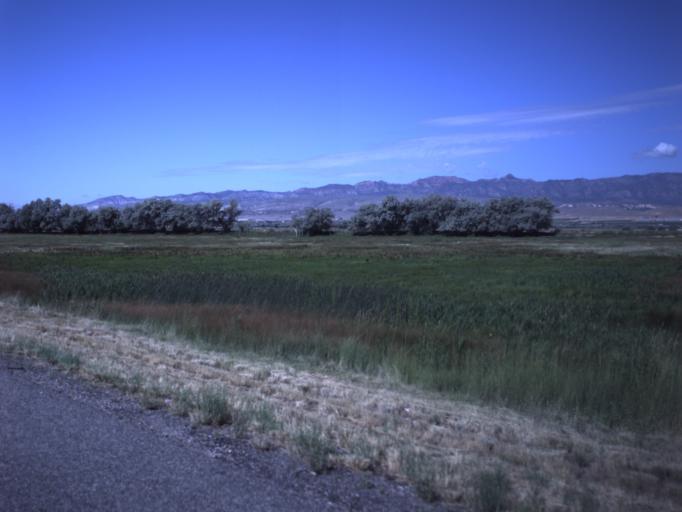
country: US
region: Utah
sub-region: Sevier County
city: Salina
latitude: 38.9820
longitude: -111.8531
